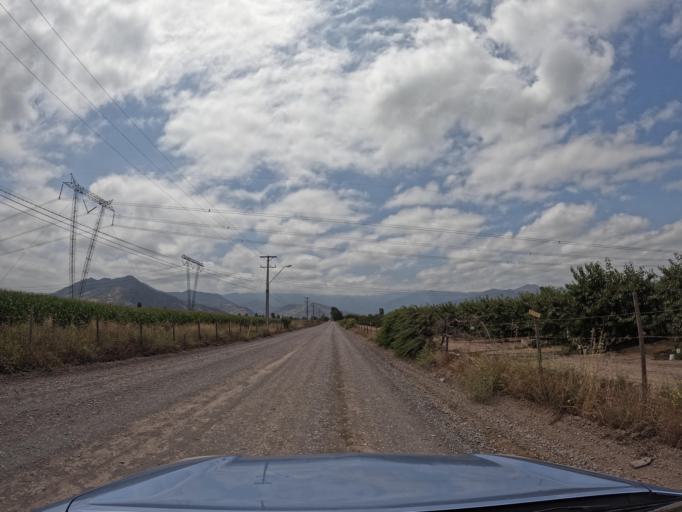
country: CL
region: O'Higgins
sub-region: Provincia de Colchagua
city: Chimbarongo
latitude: -34.7414
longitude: -70.9763
